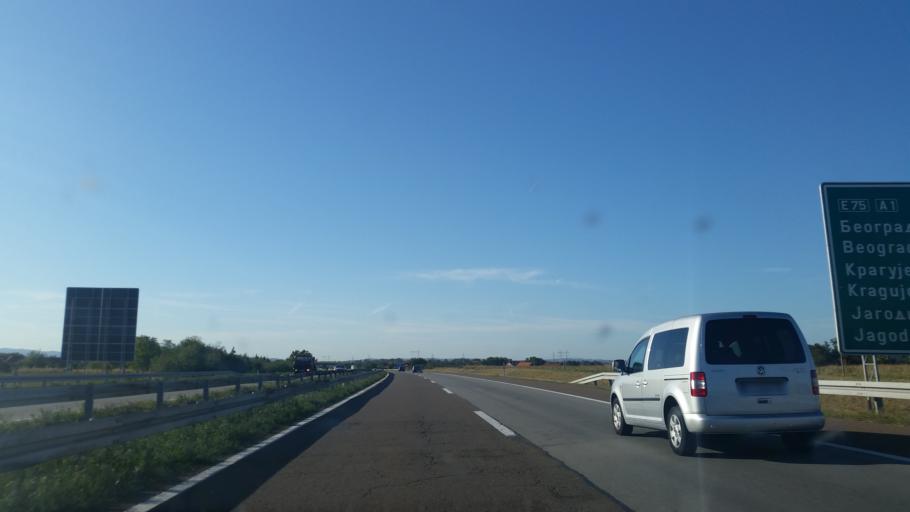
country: RS
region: Central Serbia
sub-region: Pomoravski Okrug
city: Cuprija
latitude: 43.9443
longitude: 21.3836
